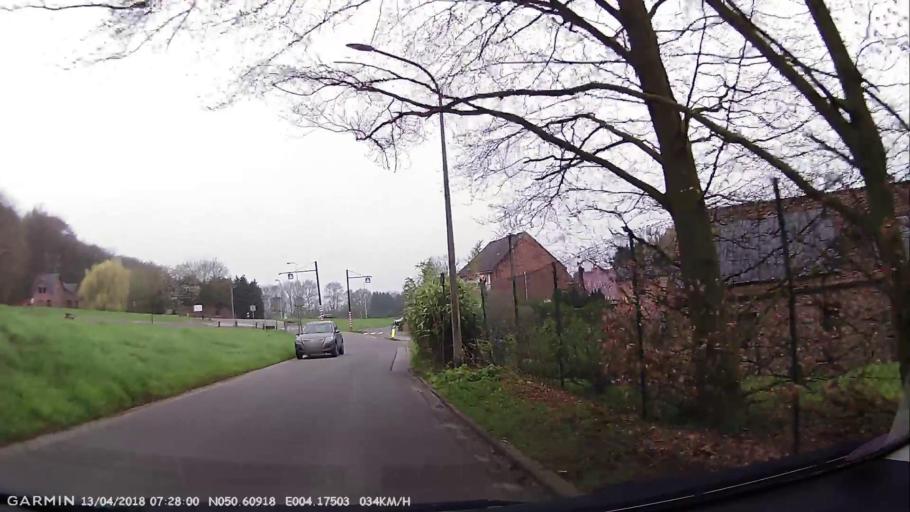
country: BE
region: Wallonia
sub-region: Province du Hainaut
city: Braine-le-Comte
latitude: 50.6091
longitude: 4.1749
